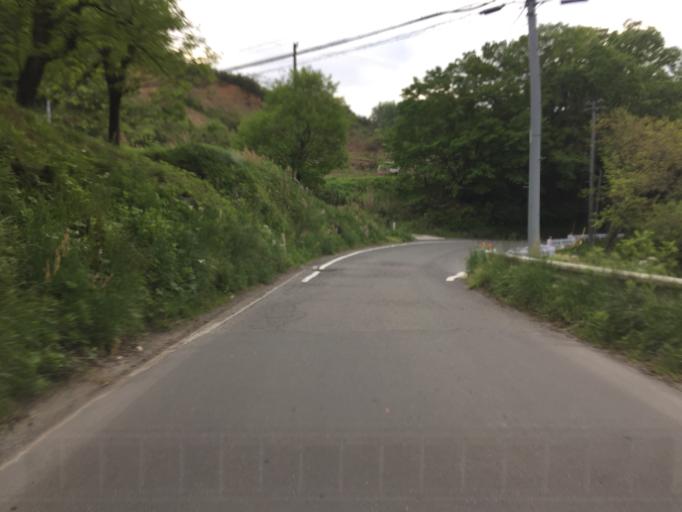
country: JP
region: Miyagi
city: Marumori
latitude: 37.9000
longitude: 140.7501
